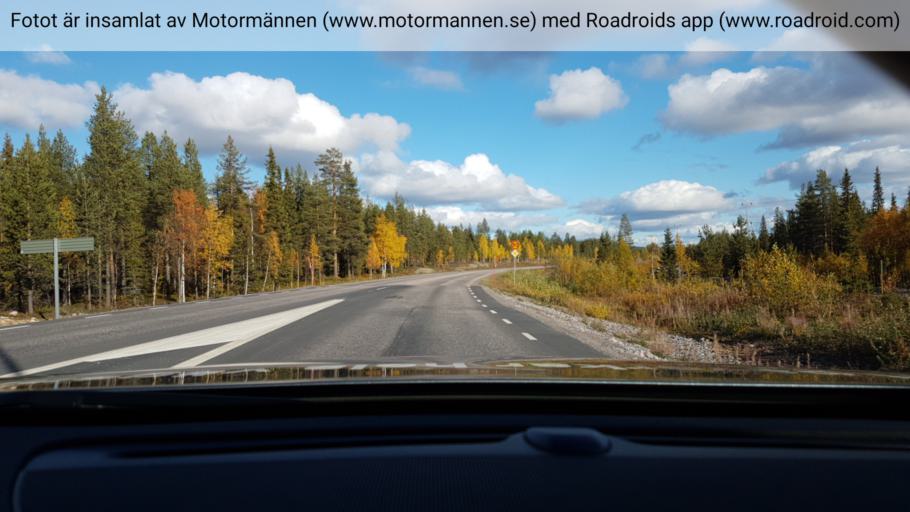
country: SE
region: Norrbotten
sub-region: Gallivare Kommun
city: Malmberget
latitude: 67.1624
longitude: 20.6915
